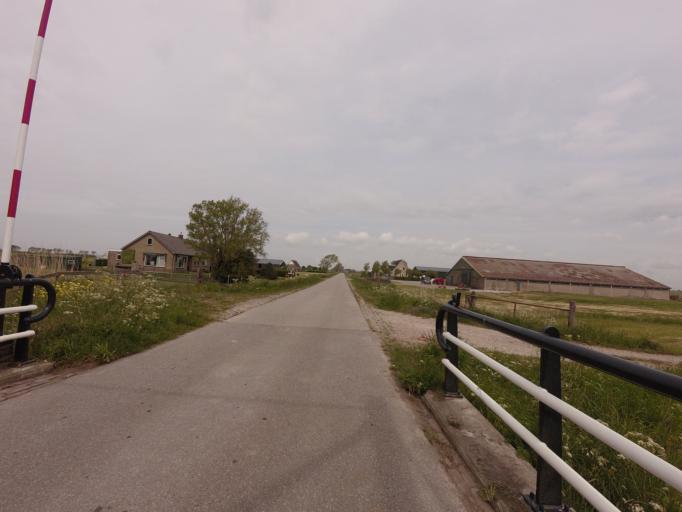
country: NL
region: Friesland
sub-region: Sudwest Fryslan
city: Makkum
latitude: 53.0633
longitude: 5.4613
